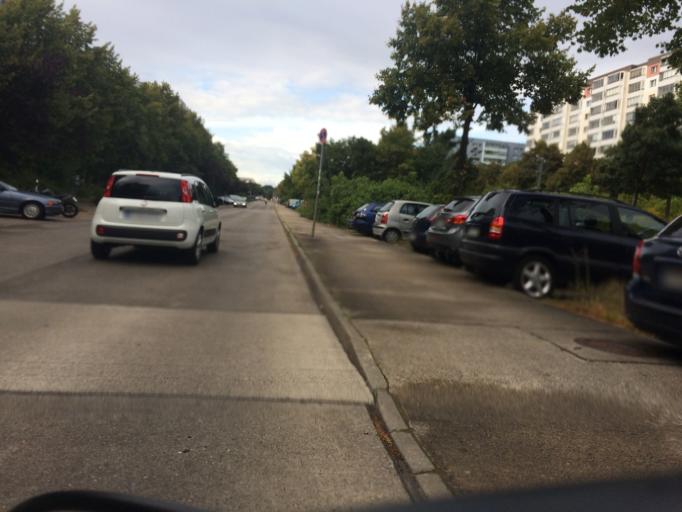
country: DE
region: Berlin
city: Neu-Hohenschoenhausen
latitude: 52.5671
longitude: 13.5005
